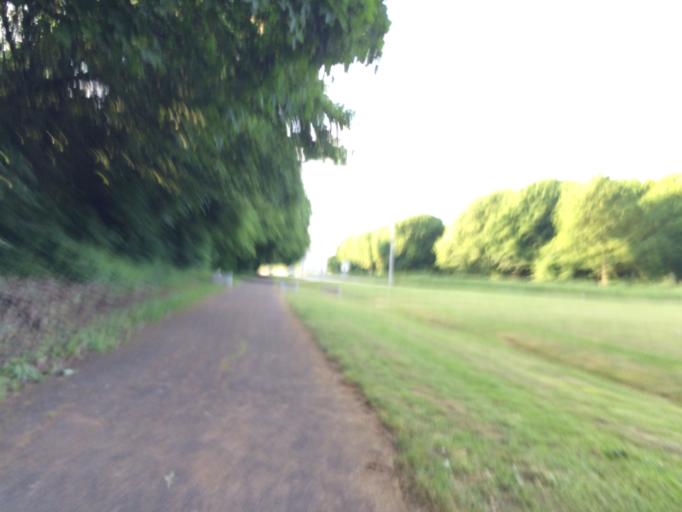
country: FR
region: Ile-de-France
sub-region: Departement de l'Essonne
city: Lisses
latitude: 48.6148
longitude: 2.4227
